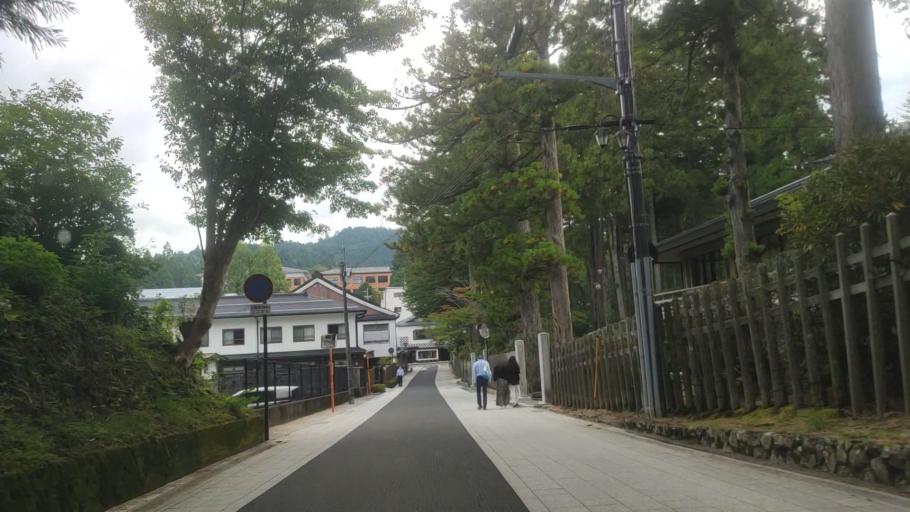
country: JP
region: Wakayama
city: Koya
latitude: 34.2143
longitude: 135.5851
